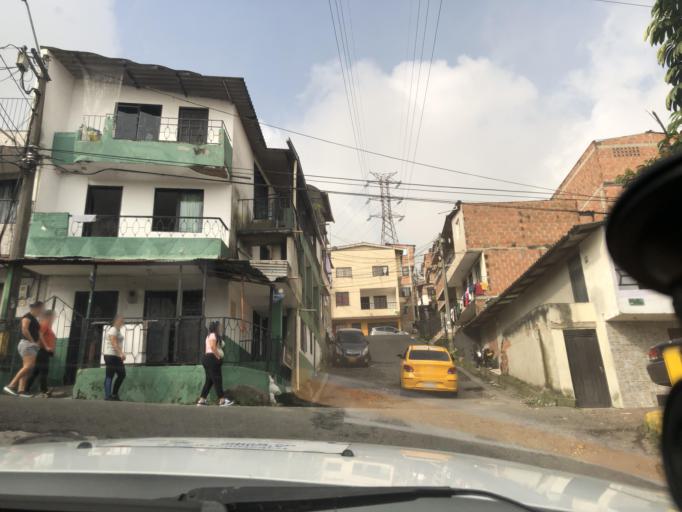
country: CO
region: Antioquia
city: Bello
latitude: 6.3130
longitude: -75.5735
